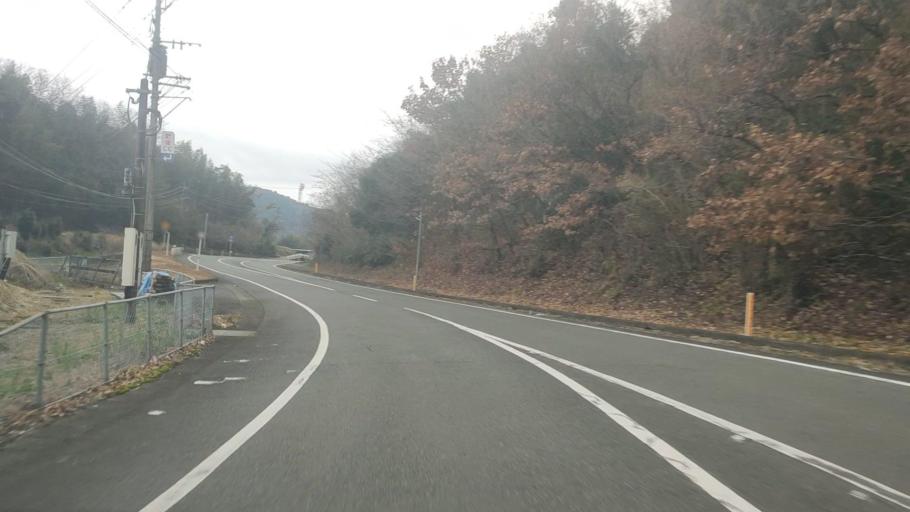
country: JP
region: Kumamoto
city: Ozu
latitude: 32.8607
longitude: 130.8960
